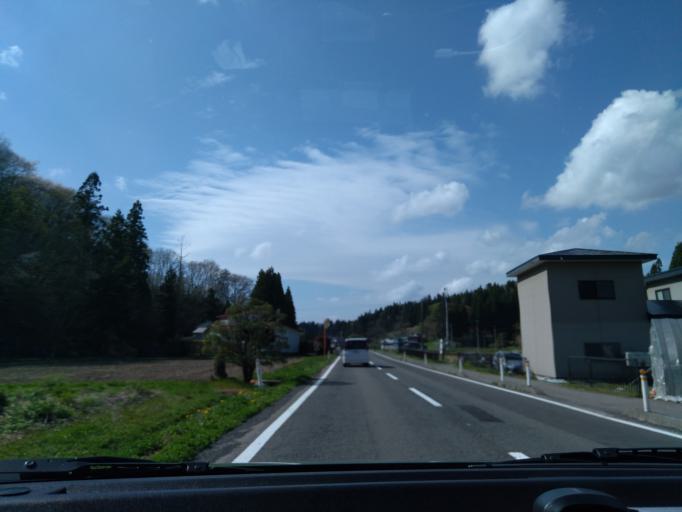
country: JP
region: Akita
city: Akita
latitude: 39.7093
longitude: 140.2052
